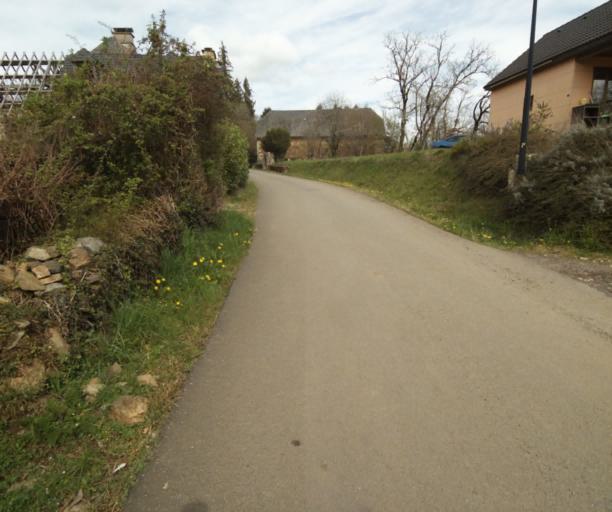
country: FR
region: Limousin
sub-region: Departement de la Correze
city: Laguenne
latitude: 45.2329
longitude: 1.8403
